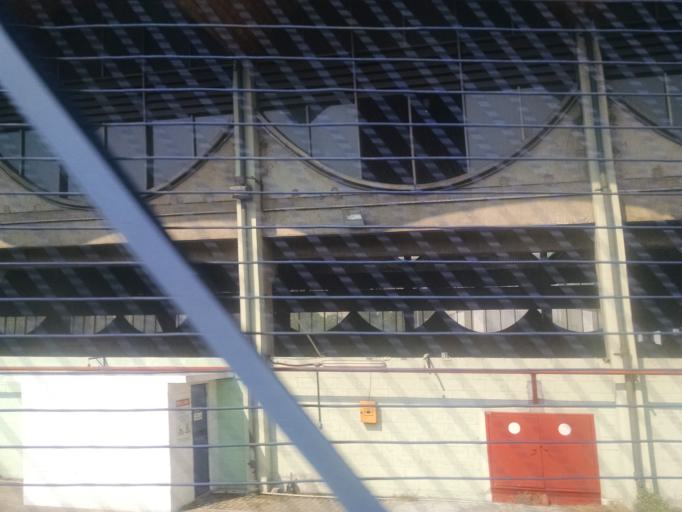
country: BR
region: Rio de Janeiro
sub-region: Rio De Janeiro
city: Rio de Janeiro
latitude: -22.9081
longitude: -43.2048
